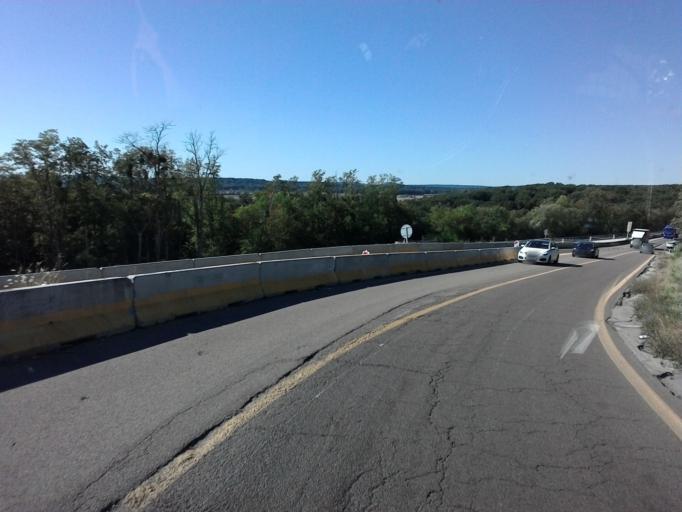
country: FR
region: Franche-Comte
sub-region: Departement du Doubs
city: Chatillon-le-Duc
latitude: 47.3196
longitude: 5.9988
